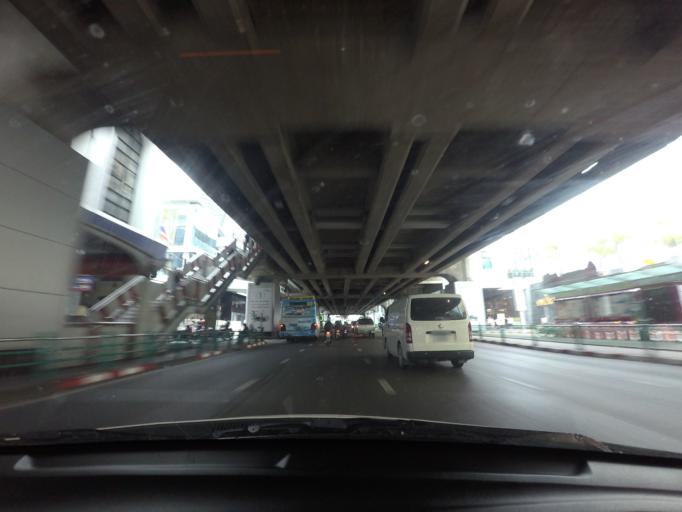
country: TH
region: Bangkok
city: Pathum Wan
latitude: 13.7449
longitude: 100.5336
